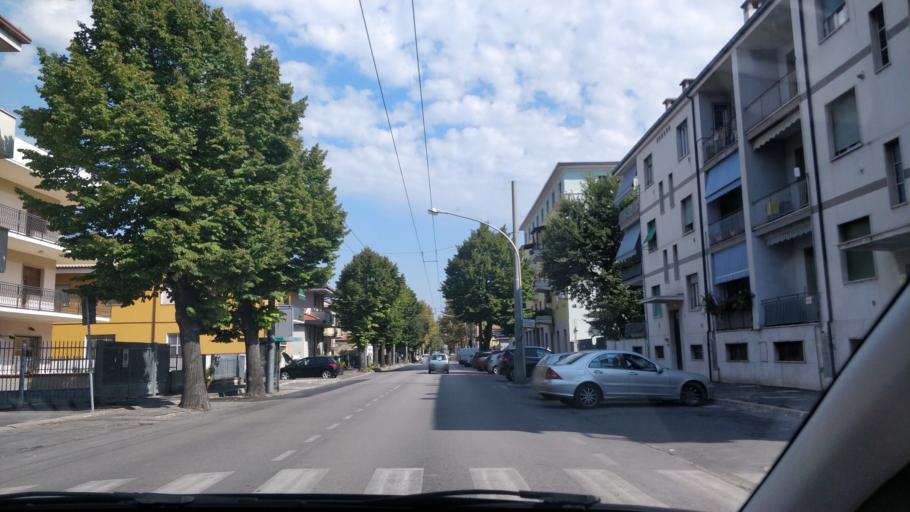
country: IT
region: Abruzzo
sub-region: Provincia di Chieti
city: Chieti
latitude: 42.3689
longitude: 14.1426
